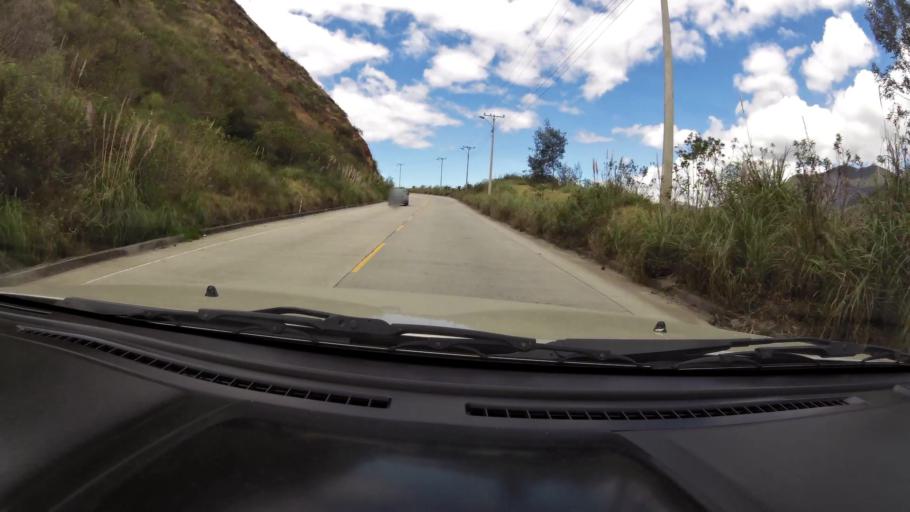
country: EC
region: Azuay
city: Cuenca
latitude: -3.1414
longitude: -79.1237
